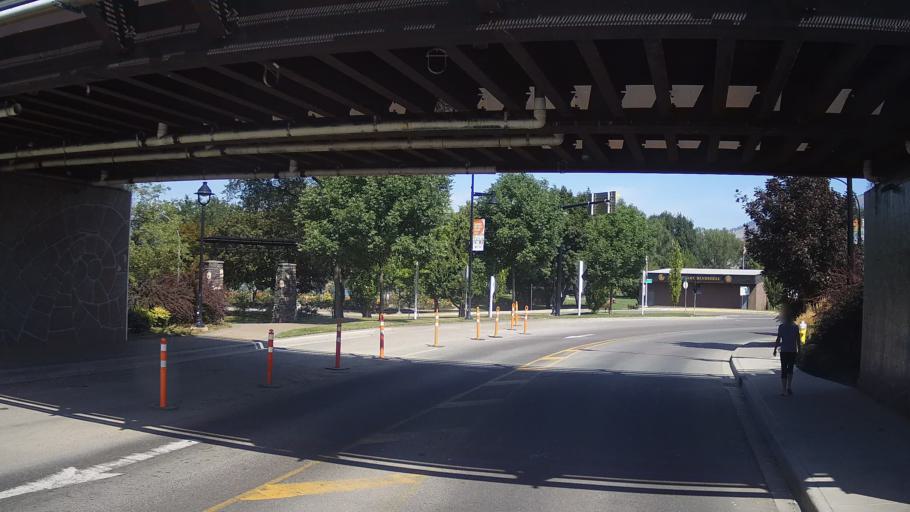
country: CA
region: British Columbia
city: Kamloops
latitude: 50.6767
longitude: -120.3392
